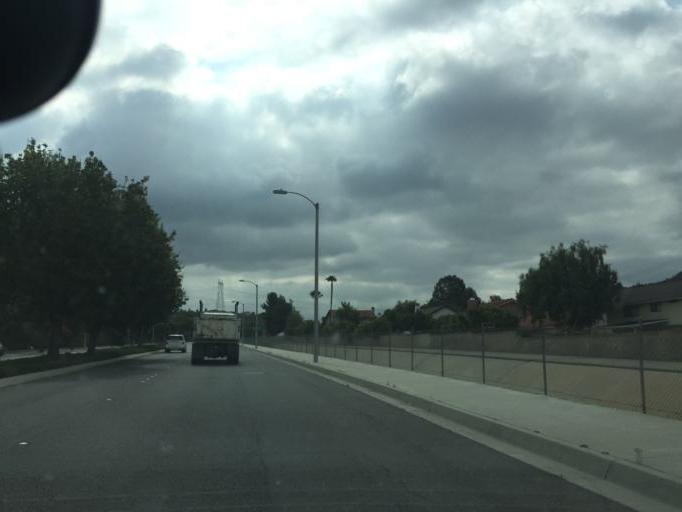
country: US
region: California
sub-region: Los Angeles County
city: Santa Clarita
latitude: 34.4490
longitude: -118.4958
